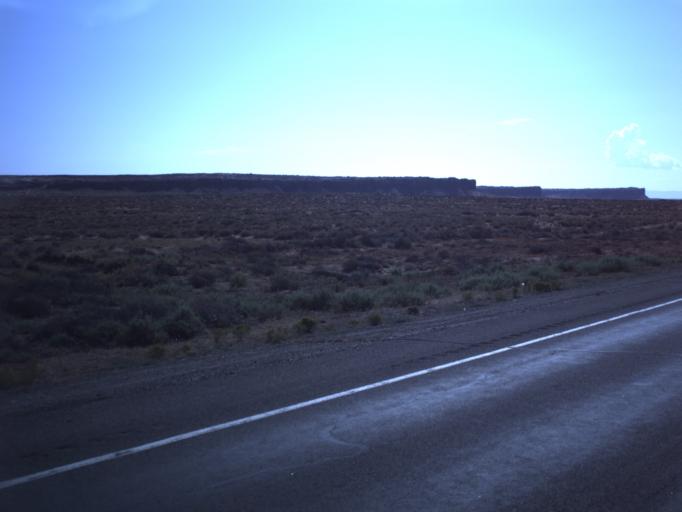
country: US
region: Utah
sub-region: San Juan County
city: Blanding
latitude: 37.2210
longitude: -109.6163
